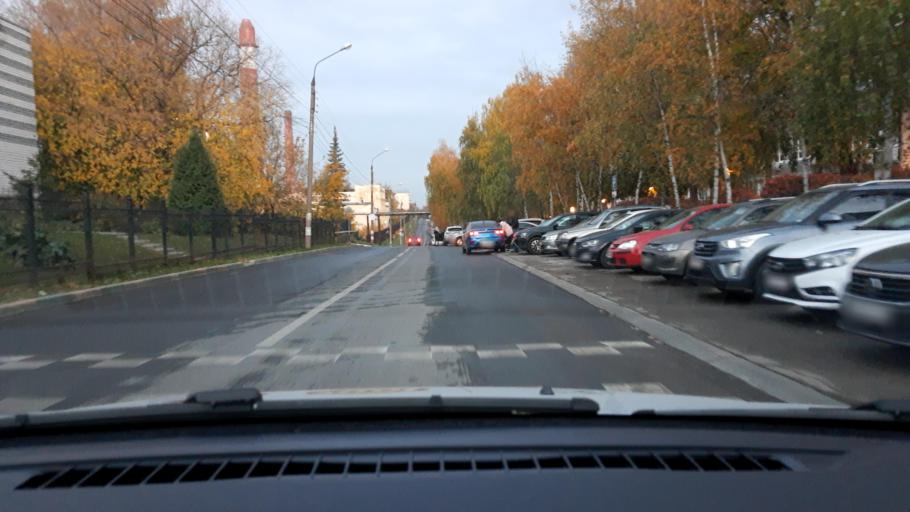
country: RU
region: Nizjnij Novgorod
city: Nizhniy Novgorod
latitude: 56.2502
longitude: 43.9770
